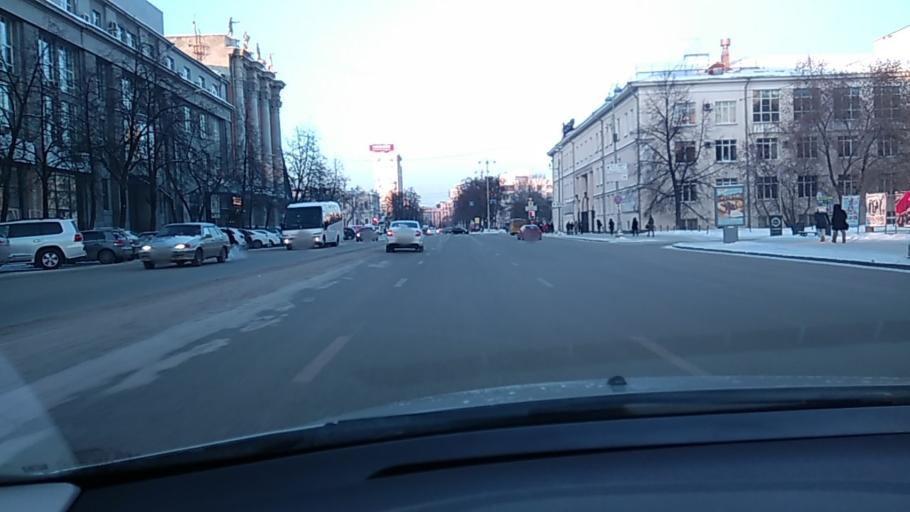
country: RU
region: Sverdlovsk
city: Yekaterinburg
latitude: 56.8365
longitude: 60.5994
